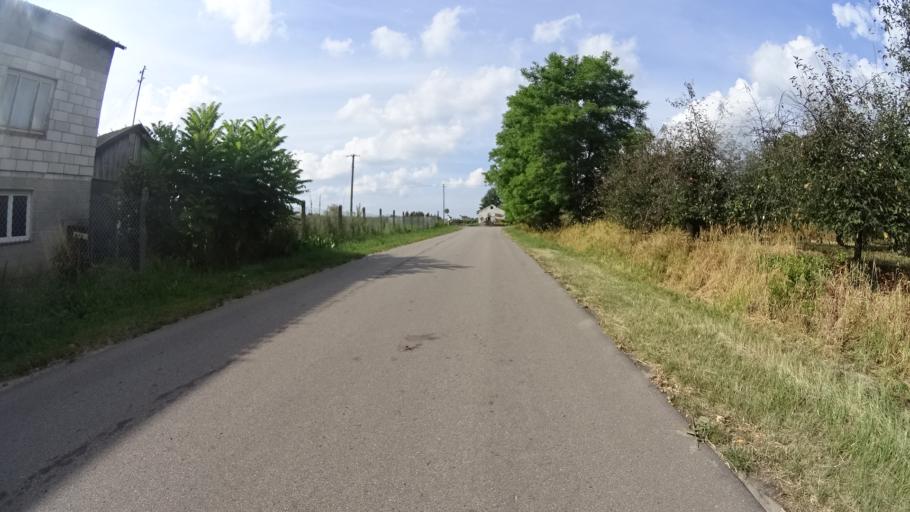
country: PL
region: Masovian Voivodeship
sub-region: Powiat grojecki
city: Goszczyn
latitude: 51.7006
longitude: 20.8469
